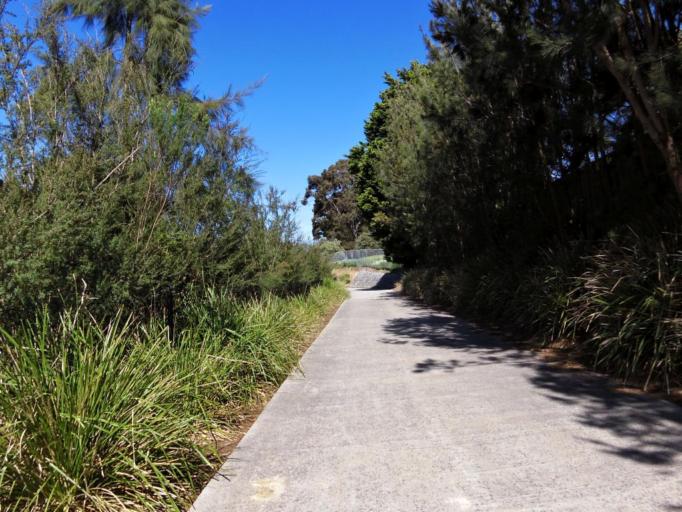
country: AU
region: Victoria
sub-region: Greater Dandenong
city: Dandenong North
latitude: -37.9696
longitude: 145.1938
